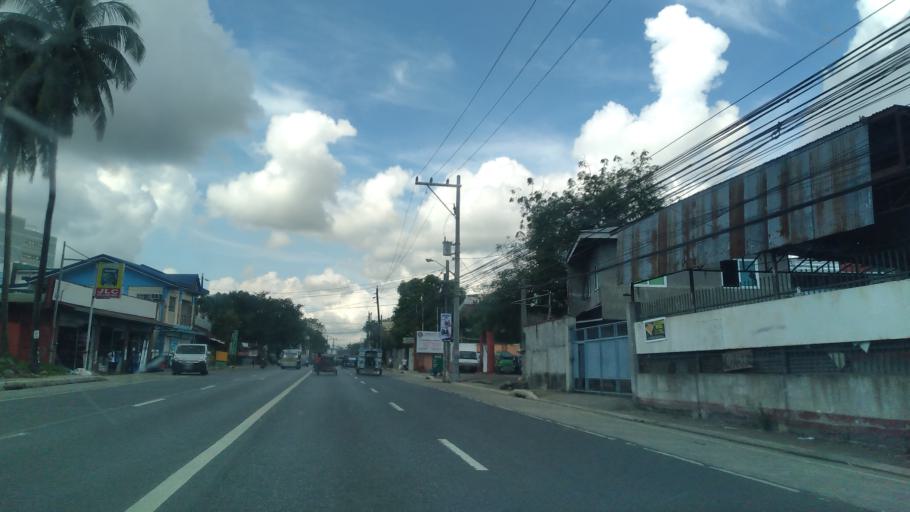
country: PH
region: Calabarzon
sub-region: Province of Quezon
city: Isabang
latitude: 13.9471
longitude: 121.5874
